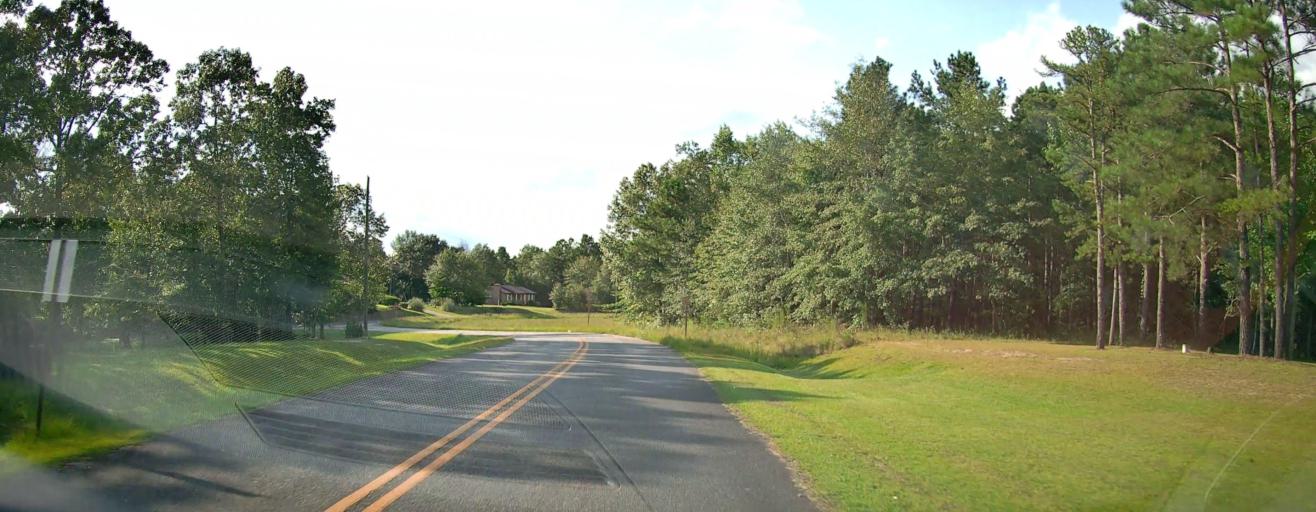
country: US
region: Georgia
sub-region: Crawford County
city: Roberta
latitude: 32.7400
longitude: -84.0147
